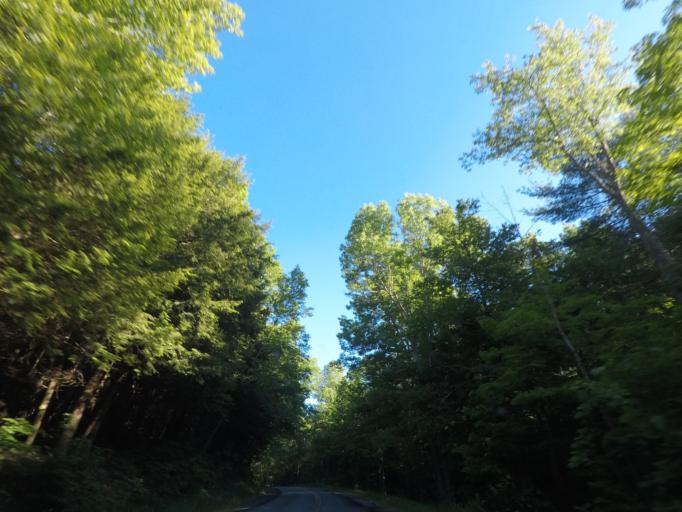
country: US
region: New York
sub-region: Rensselaer County
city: Averill Park
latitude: 42.5612
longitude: -73.5322
